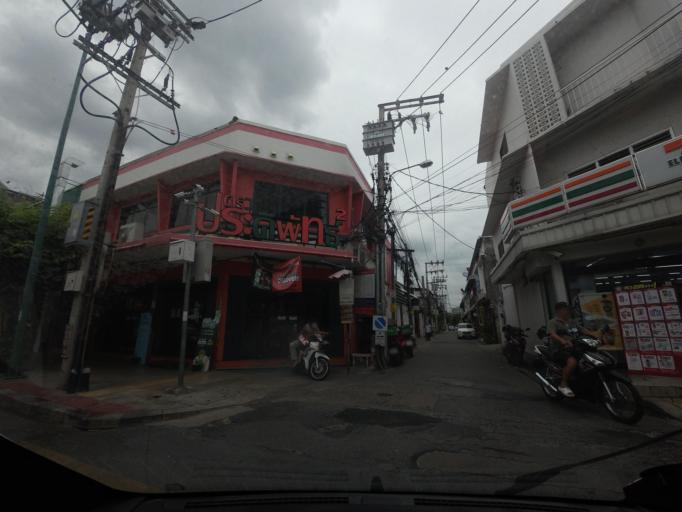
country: TH
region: Bangkok
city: Phaya Thai
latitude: 13.7914
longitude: 100.5403
